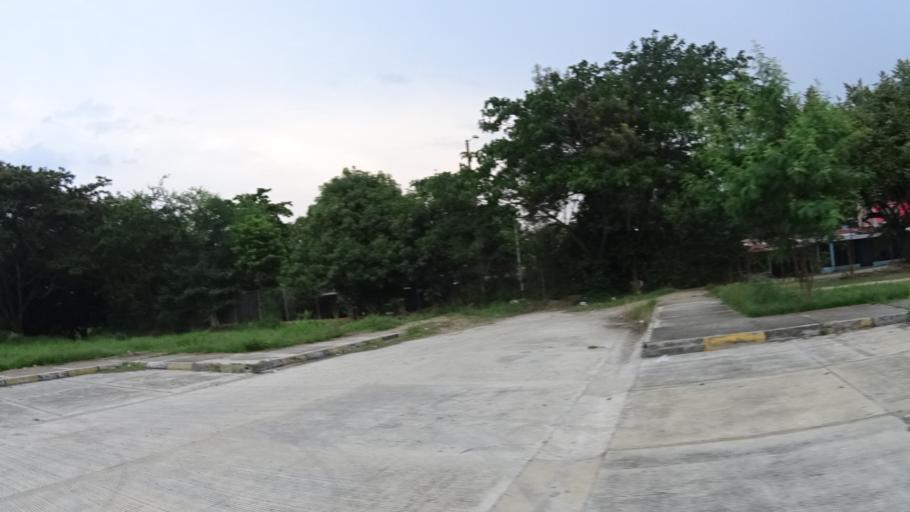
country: CO
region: Cundinamarca
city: Puerto Salgar
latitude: 5.4810
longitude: -74.6763
